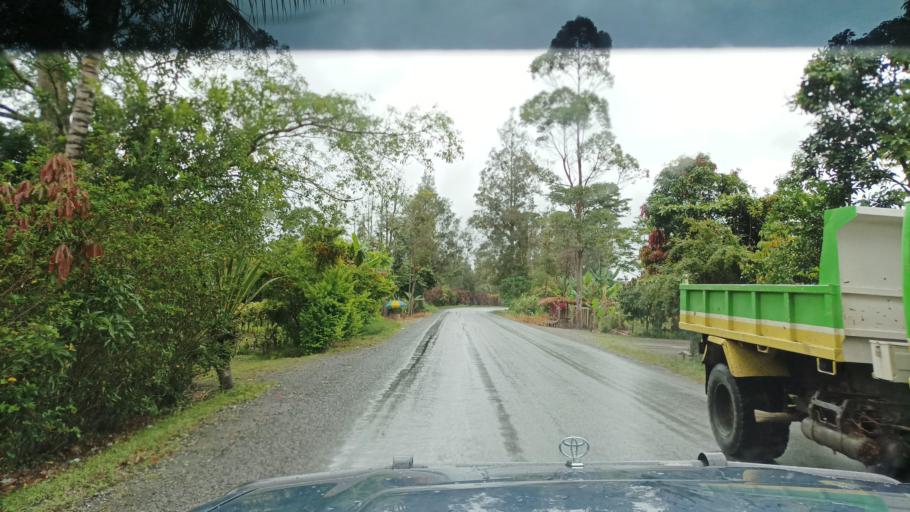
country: PG
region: Jiwaka
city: Minj
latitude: -5.8414
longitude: 144.6126
